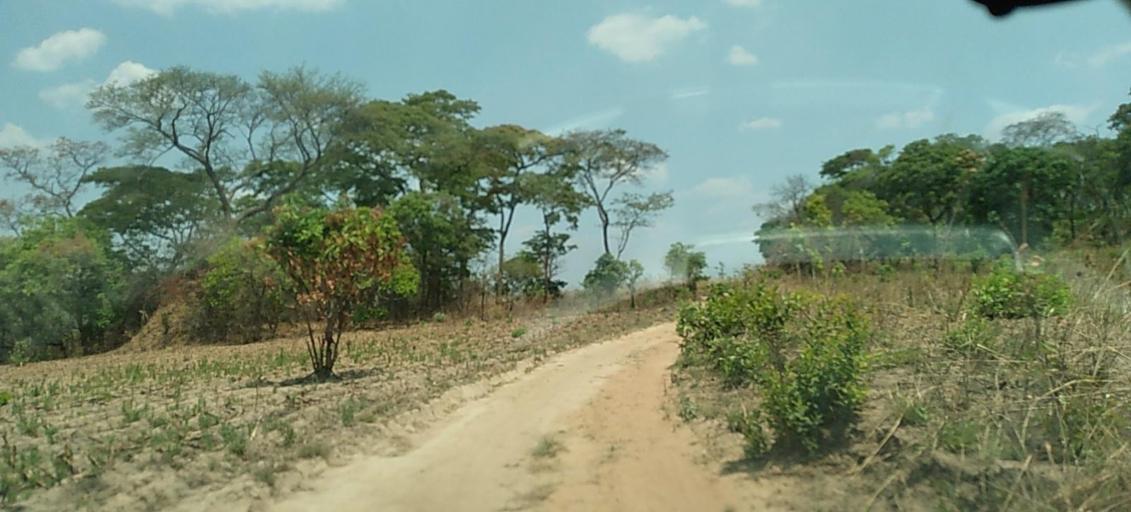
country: ZM
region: North-Western
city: Kasempa
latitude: -13.5298
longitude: 25.8229
